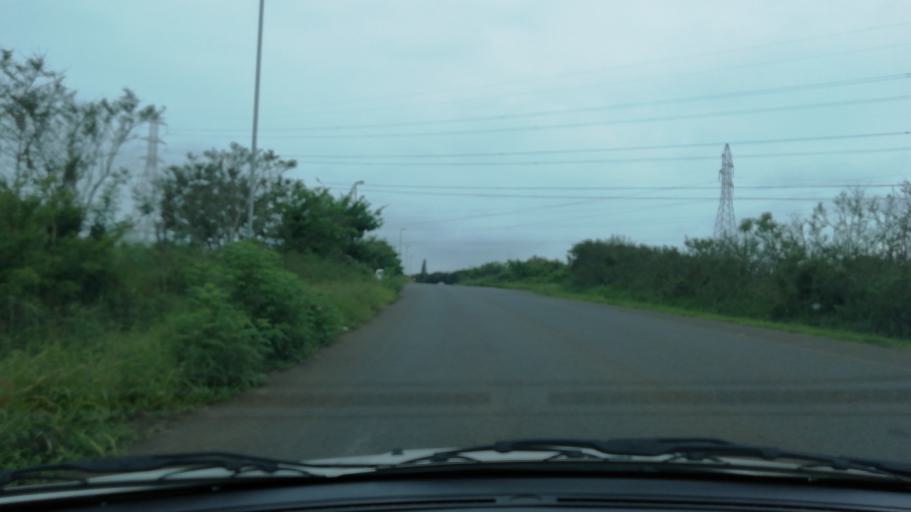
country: ZA
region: KwaZulu-Natal
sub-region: uThungulu District Municipality
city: Empangeni
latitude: -28.7355
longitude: 31.8896
